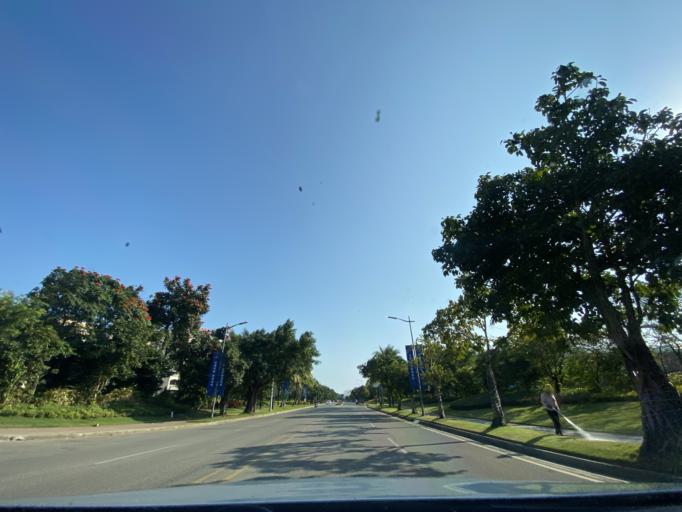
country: CN
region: Hainan
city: Xincun
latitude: 18.4186
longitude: 109.9611
